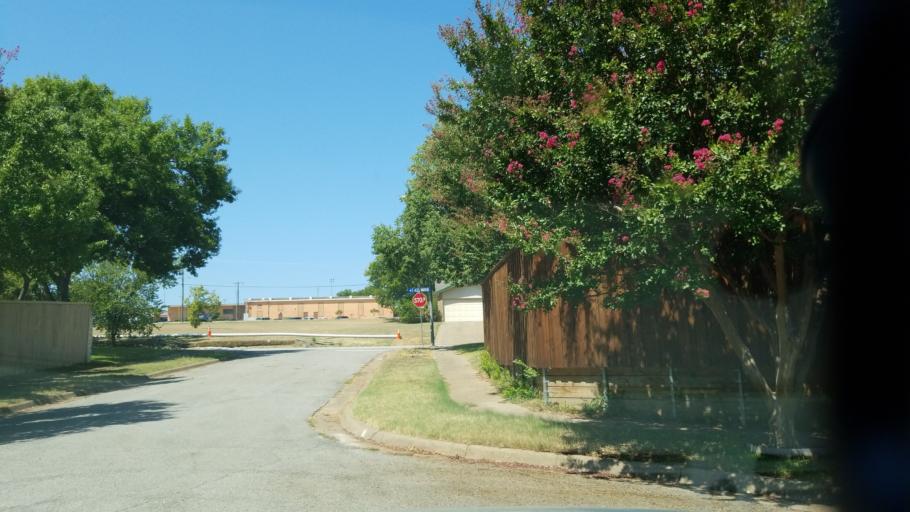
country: US
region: Texas
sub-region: Dallas County
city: Duncanville
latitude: 32.6491
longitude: -96.8985
